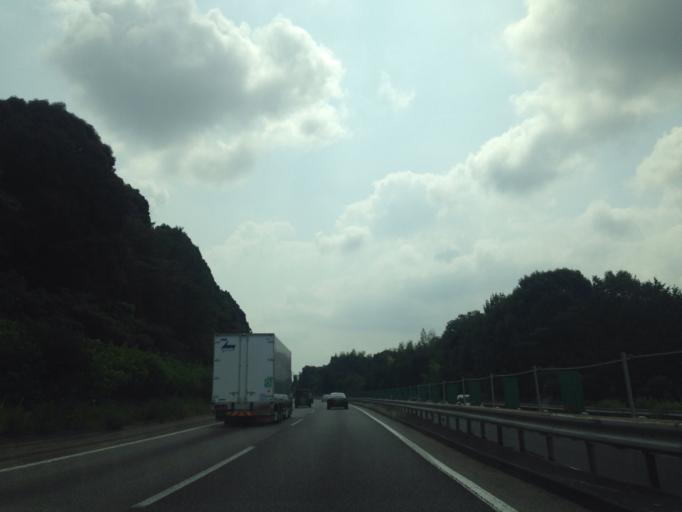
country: JP
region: Aichi
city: Gamagori
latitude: 34.8779
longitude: 137.2753
